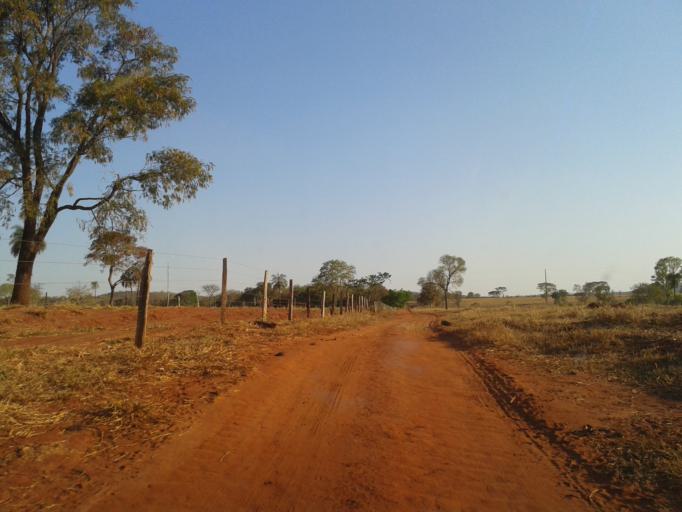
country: BR
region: Minas Gerais
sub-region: Ituiutaba
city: Ituiutaba
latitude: -19.2481
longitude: -49.6093
